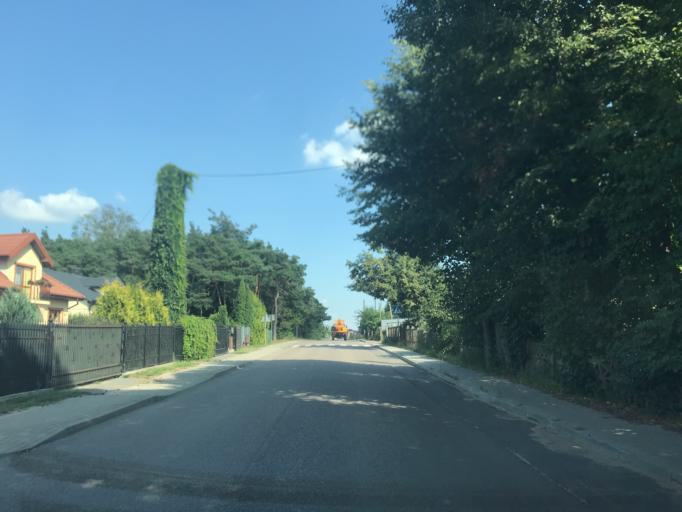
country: PL
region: Masovian Voivodeship
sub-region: Powiat mlawski
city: Mlawa
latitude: 53.1093
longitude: 20.3442
